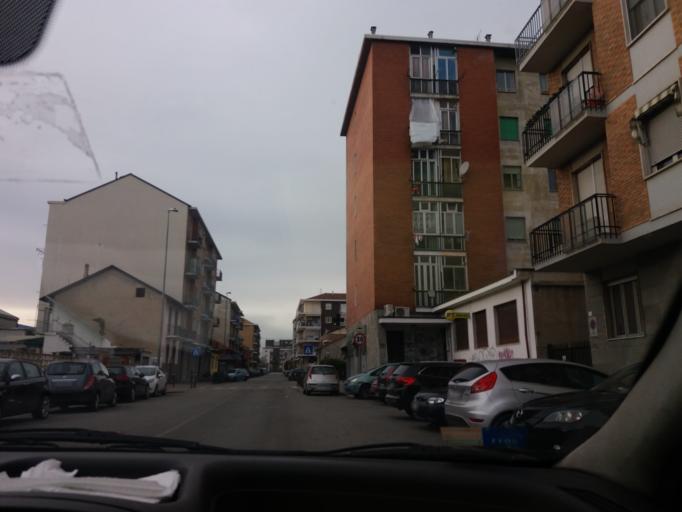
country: IT
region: Piedmont
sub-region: Provincia di Torino
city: Lesna
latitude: 45.0554
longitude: 7.6241
